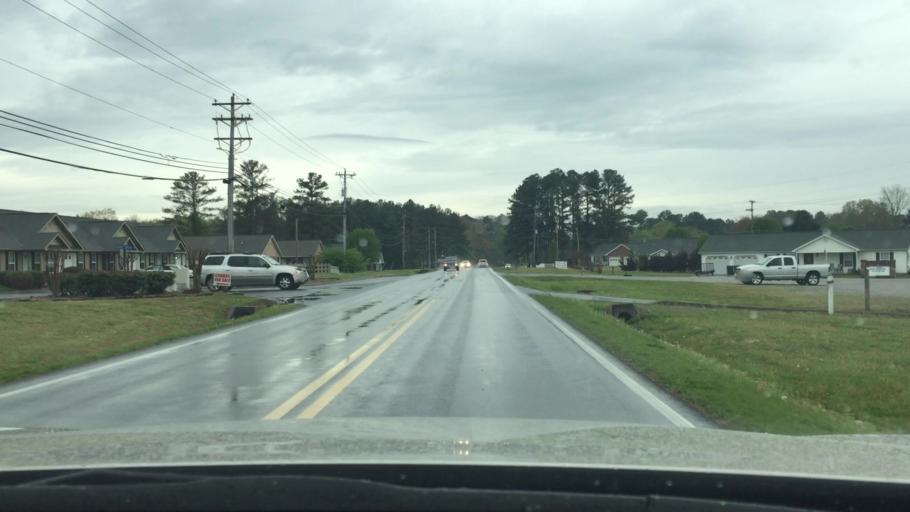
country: US
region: Georgia
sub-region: Catoosa County
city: Lakeview
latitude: 34.9683
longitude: -85.2345
